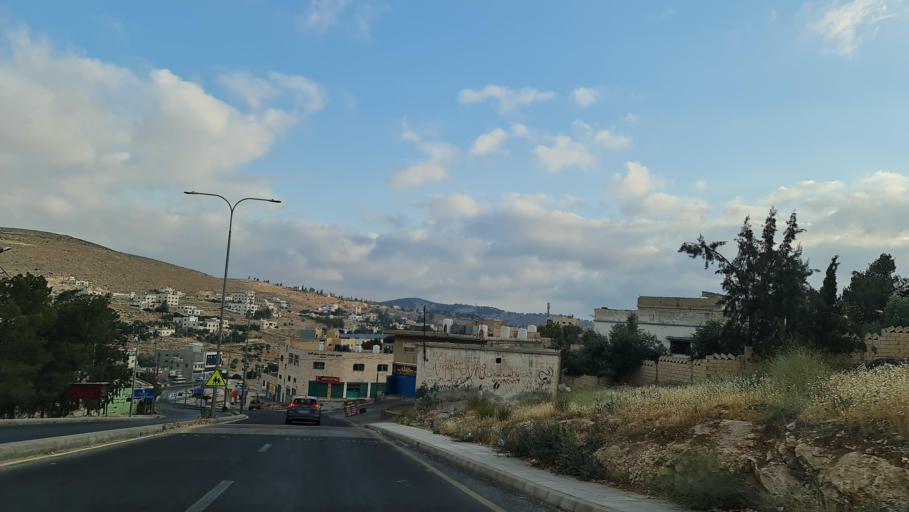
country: JO
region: Amman
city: Al Jubayhah
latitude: 32.0945
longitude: 35.9579
